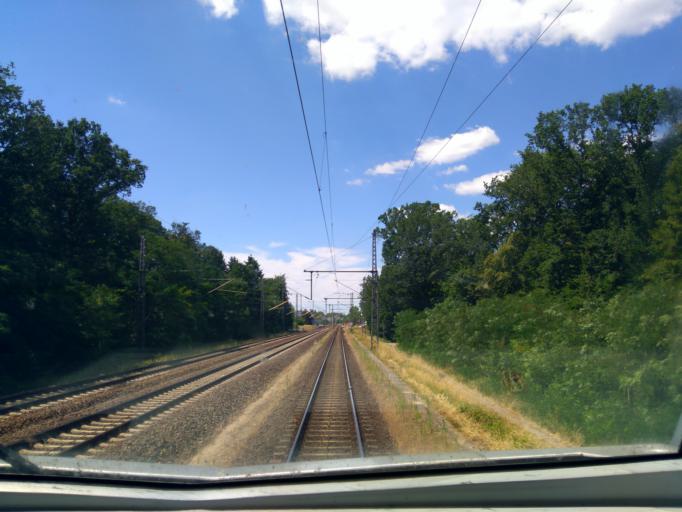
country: DE
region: Brandenburg
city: Bad Wilsnack
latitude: 52.9581
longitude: 11.9545
